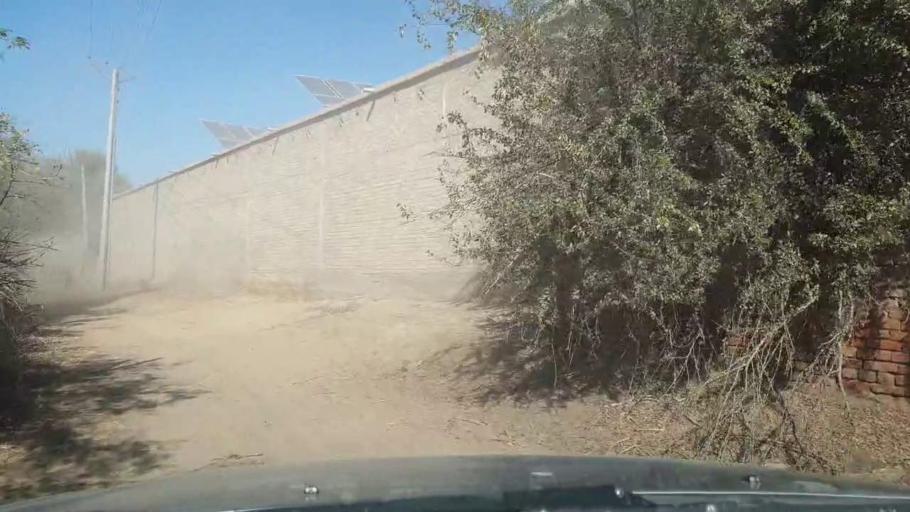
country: PK
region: Sindh
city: Ghotki
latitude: 28.0526
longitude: 69.2298
